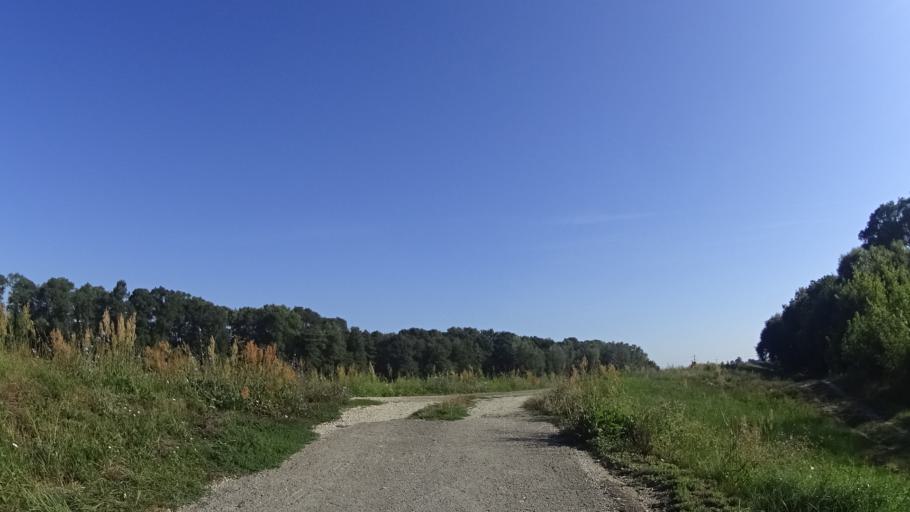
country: CZ
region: South Moravian
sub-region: Okres Breclav
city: Lanzhot
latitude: 48.7110
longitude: 17.0014
